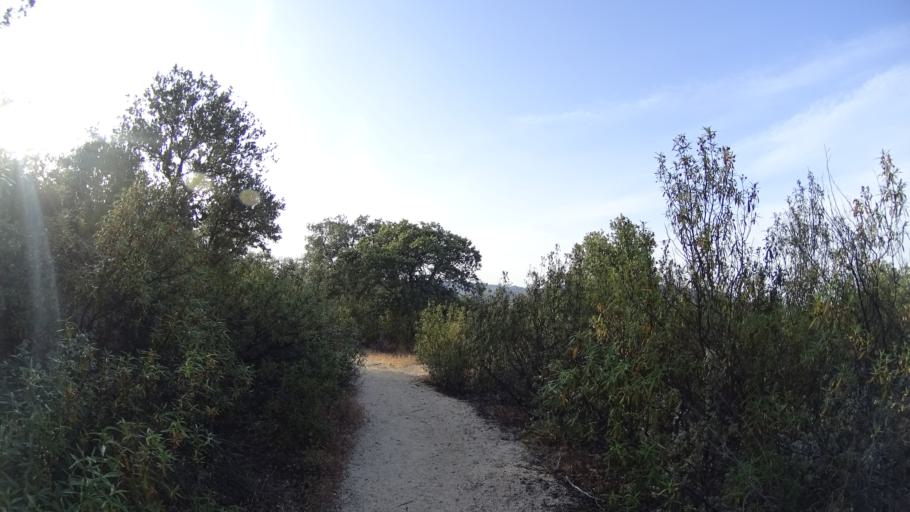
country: ES
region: Madrid
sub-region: Provincia de Madrid
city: Torrelodones
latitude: 40.5915
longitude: -3.9405
